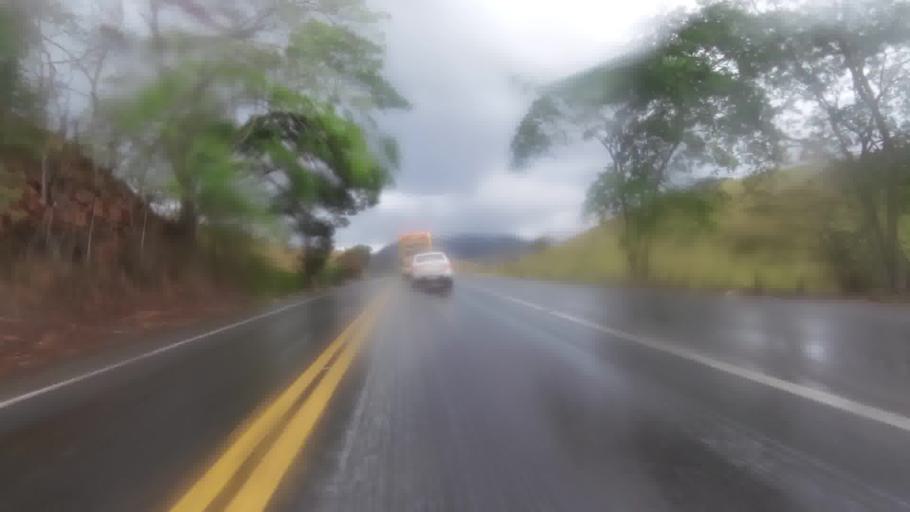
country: BR
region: Espirito Santo
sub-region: Cachoeiro De Itapemirim
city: Cachoeiro de Itapemirim
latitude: -20.9549
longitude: -41.0942
